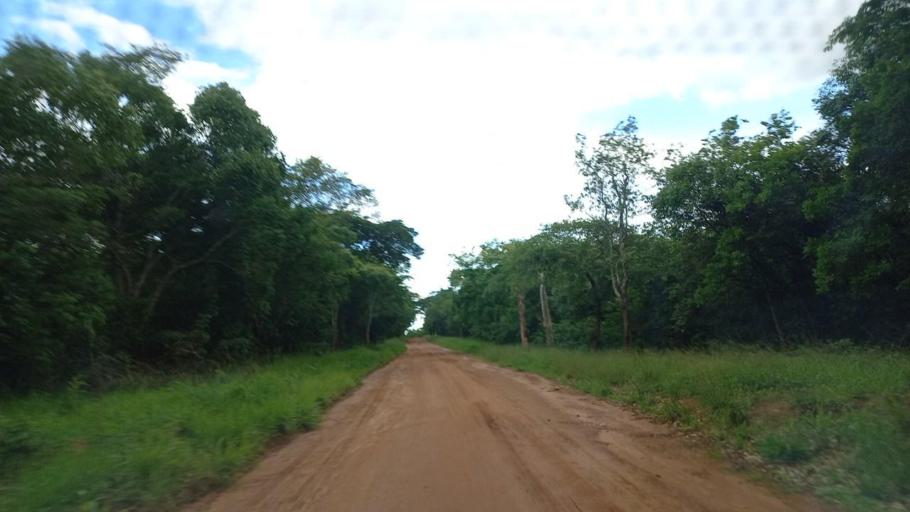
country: ZM
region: North-Western
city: Mwinilunga
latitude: -11.8337
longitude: 24.3692
